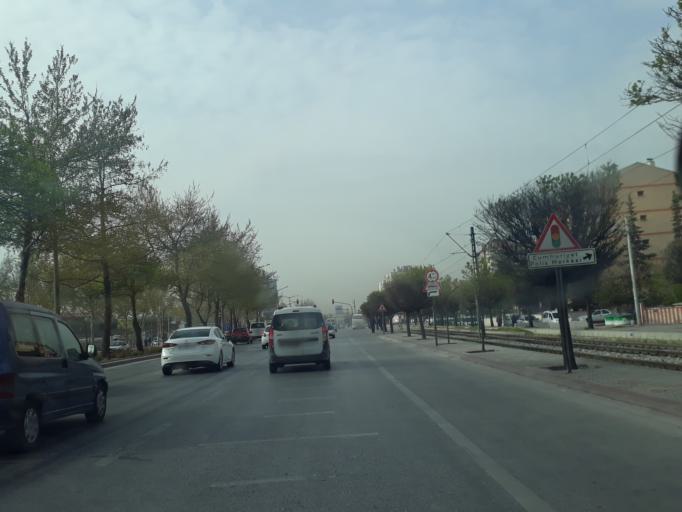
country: TR
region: Konya
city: Selcuklu
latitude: 37.9434
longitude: 32.5119
